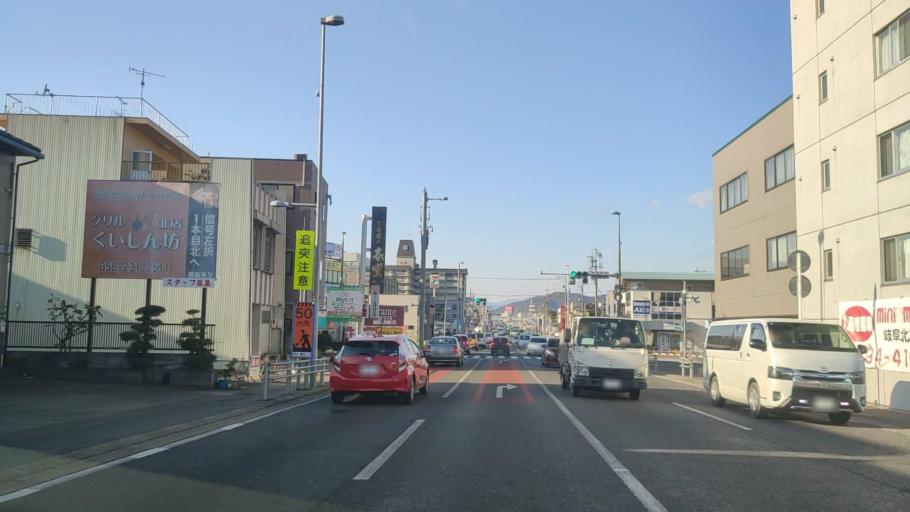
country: JP
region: Gifu
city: Gifu-shi
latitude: 35.4335
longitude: 136.7493
